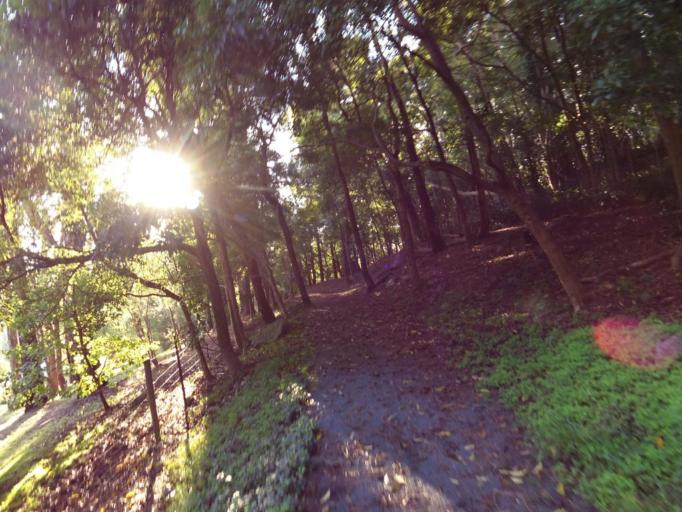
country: AU
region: Victoria
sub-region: Yarra Ranges
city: Mount Evelyn
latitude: -37.7855
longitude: 145.3652
